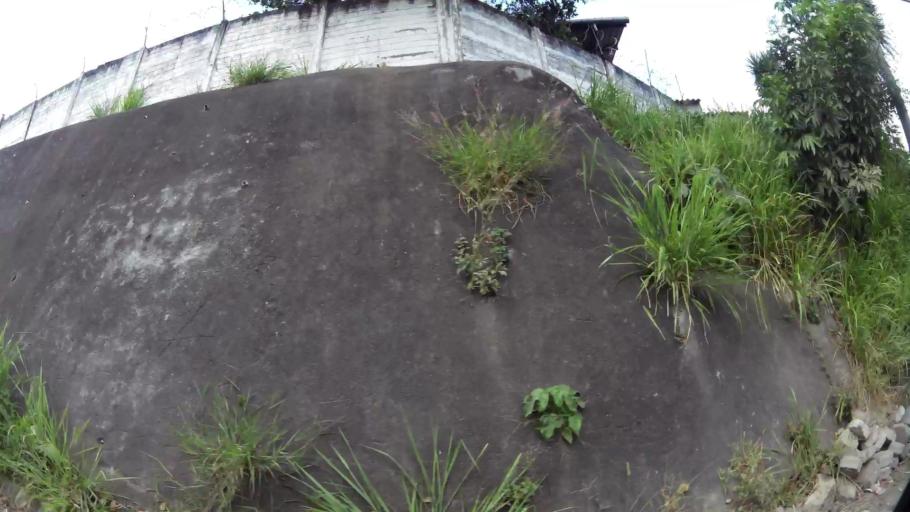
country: SV
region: San Salvador
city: Mejicanos
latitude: 13.7149
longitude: -89.2483
